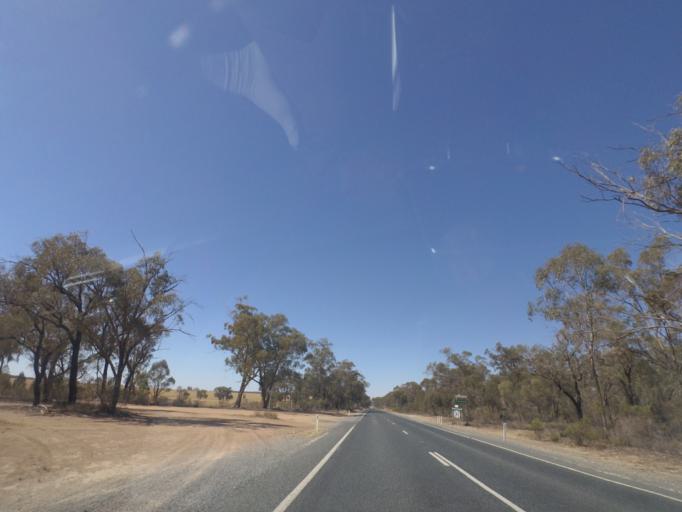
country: AU
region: New South Wales
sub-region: Bland
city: West Wyalong
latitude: -34.1424
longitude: 147.1199
